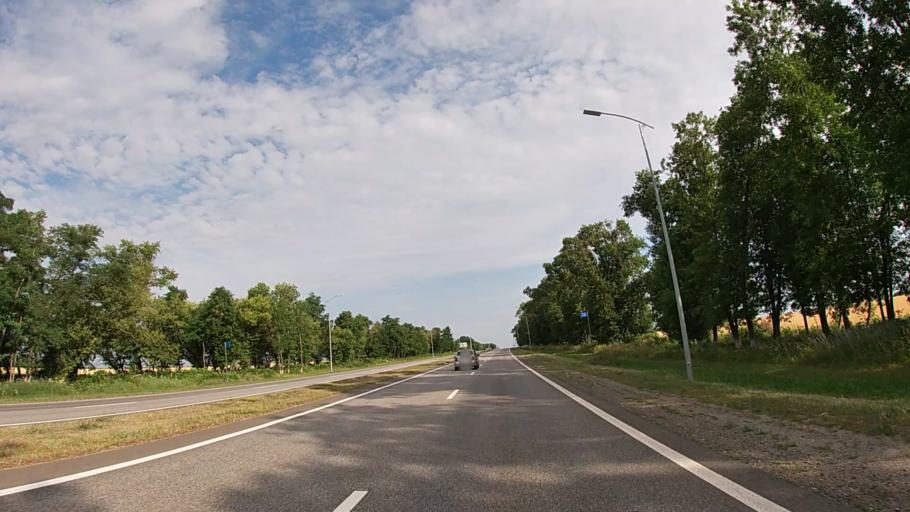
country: RU
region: Belgorod
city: Tomarovka
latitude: 50.6761
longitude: 36.2931
